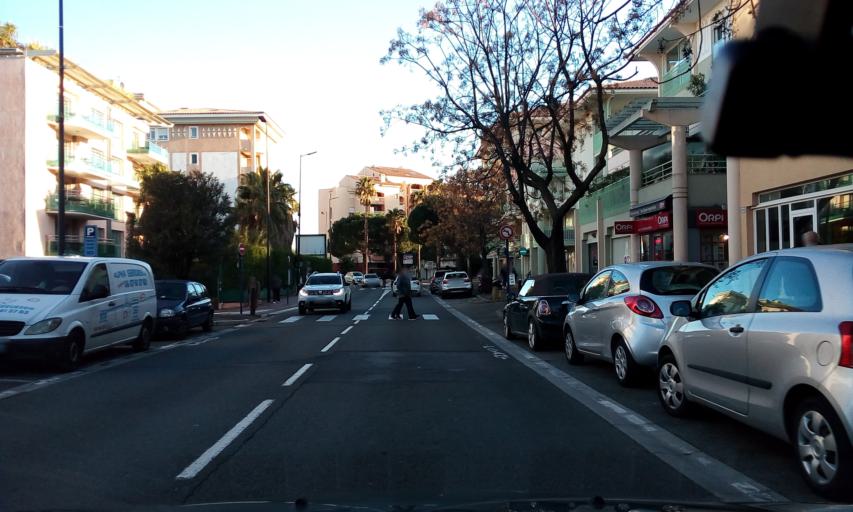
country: FR
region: Provence-Alpes-Cote d'Azur
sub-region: Departement du Var
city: Frejus
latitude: 43.4231
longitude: 6.7497
